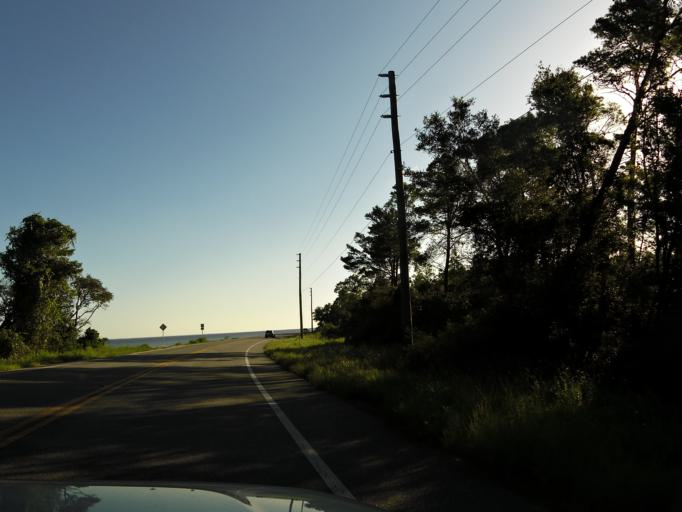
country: US
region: Florida
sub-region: Franklin County
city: Eastpoint
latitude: 29.7865
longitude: -84.7675
